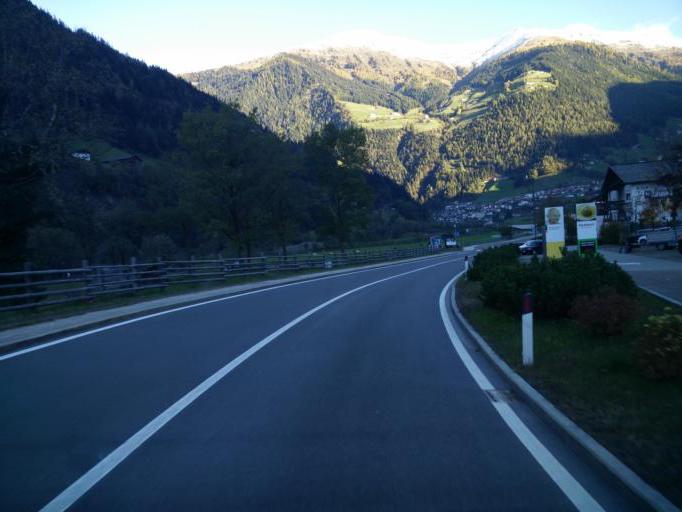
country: IT
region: Trentino-Alto Adige
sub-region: Bolzano
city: San Leonardo in Passiria
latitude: 46.8005
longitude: 11.2379
